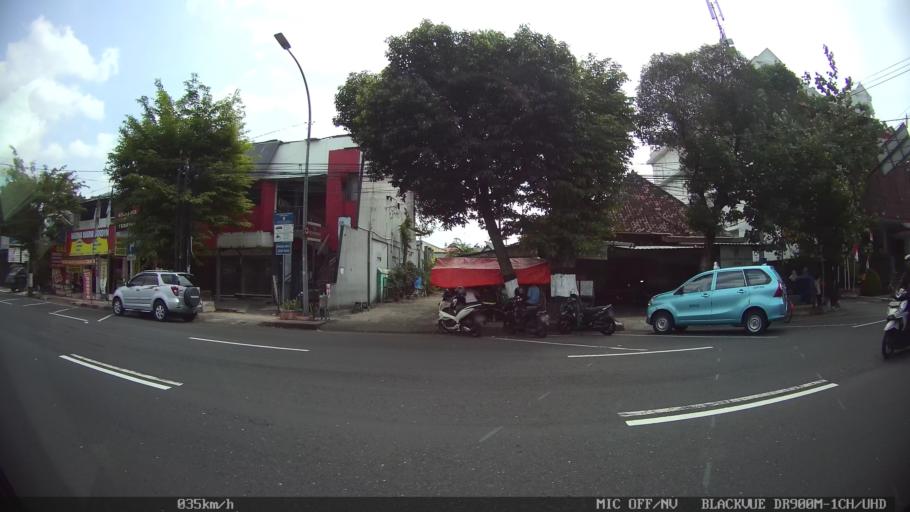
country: ID
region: Daerah Istimewa Yogyakarta
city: Yogyakarta
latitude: -7.7835
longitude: 110.3852
